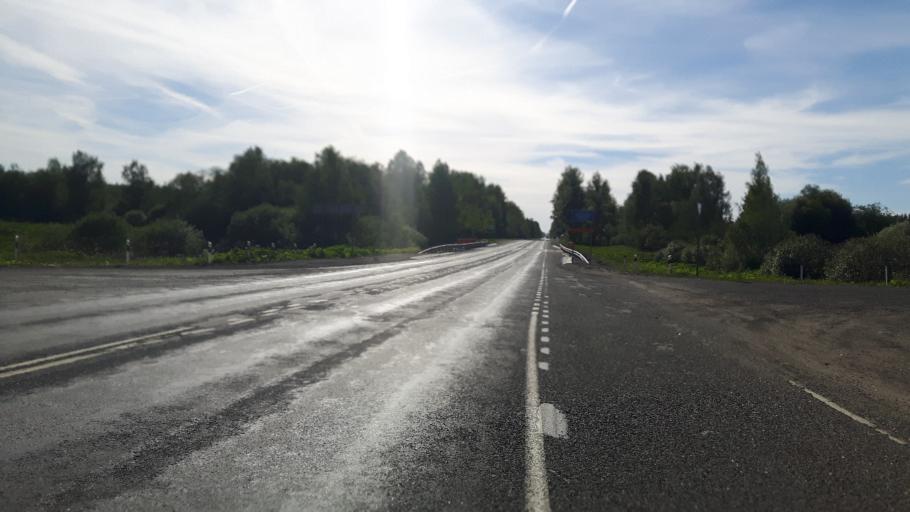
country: RU
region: Leningrad
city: Ivangorod
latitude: 59.3809
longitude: 28.3296
